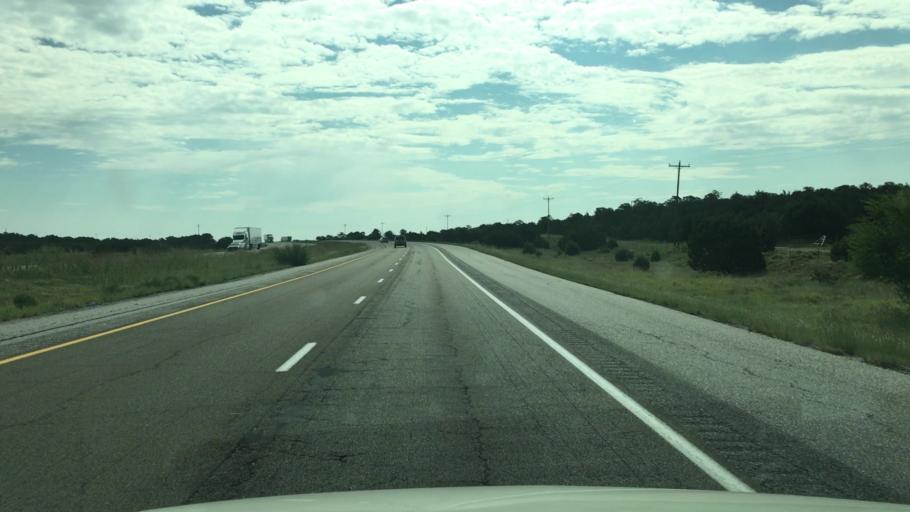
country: US
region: New Mexico
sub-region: Torrance County
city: Moriarty
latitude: 35.0018
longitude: -105.5567
